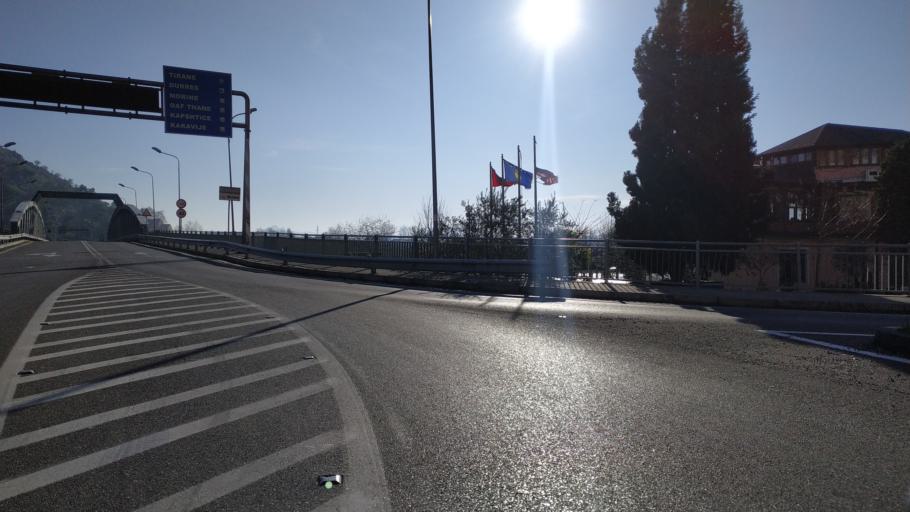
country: AL
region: Shkoder
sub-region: Rrethi i Shkodres
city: Berdica e Madhe
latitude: 42.0462
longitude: 19.4856
